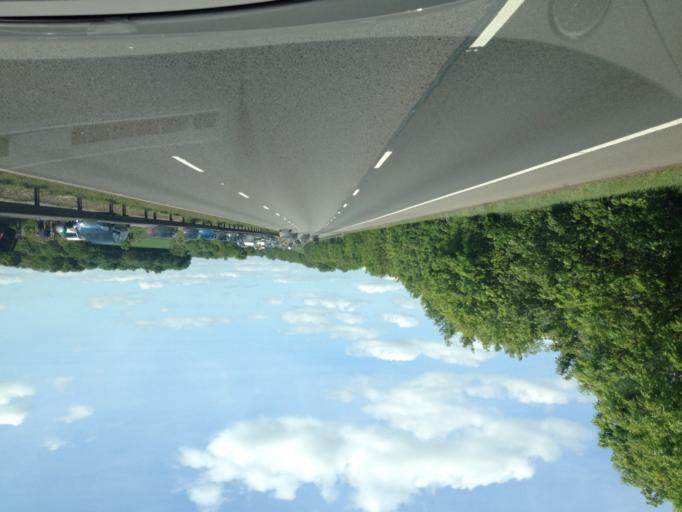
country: GB
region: England
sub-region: Oxfordshire
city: Thame
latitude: 51.7035
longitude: -0.9982
